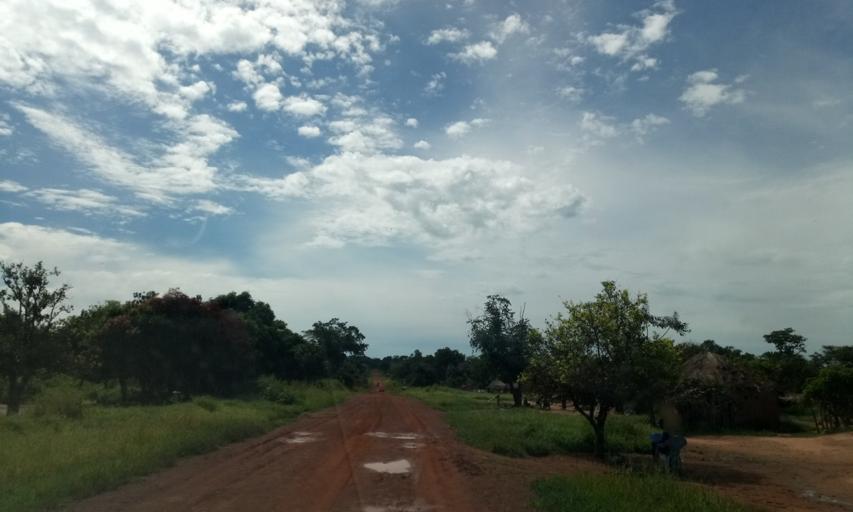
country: ZM
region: Luapula
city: Mwense
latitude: -10.6784
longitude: 28.1549
